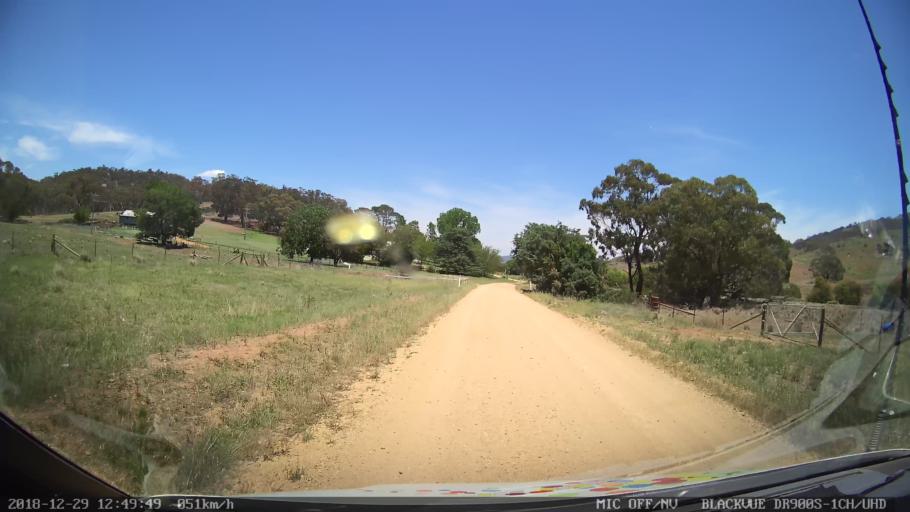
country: AU
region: Australian Capital Territory
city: Macarthur
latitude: -35.6665
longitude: 149.2053
